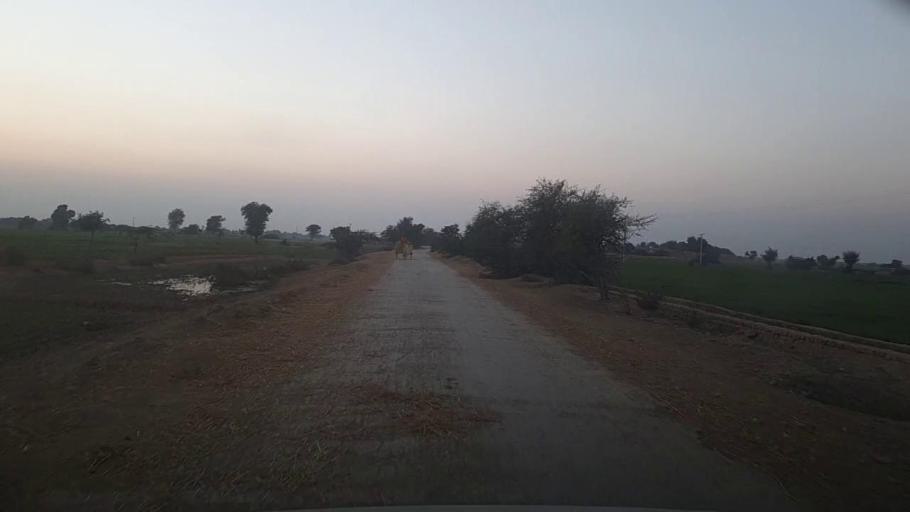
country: PK
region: Sindh
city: Khairpur Nathan Shah
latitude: 27.1815
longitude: 67.6013
